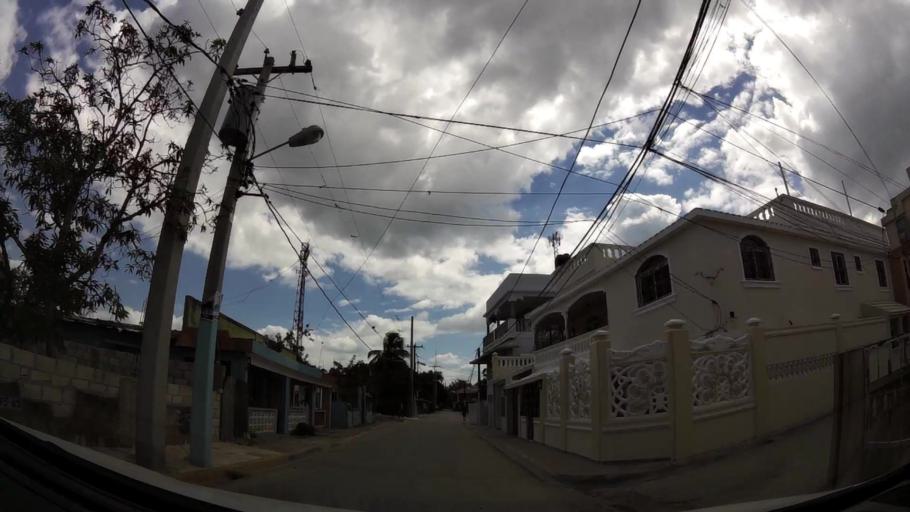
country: DO
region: Santo Domingo
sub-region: Santo Domingo
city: Boca Chica
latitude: 18.4484
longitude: -69.6370
